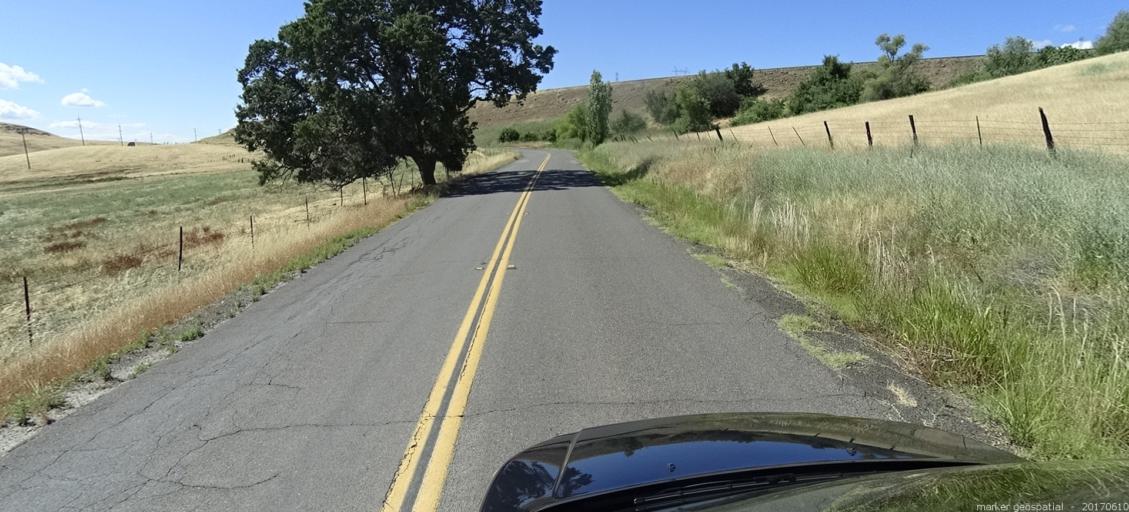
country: US
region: California
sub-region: Butte County
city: Thermalito
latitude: 39.5407
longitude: -121.5841
